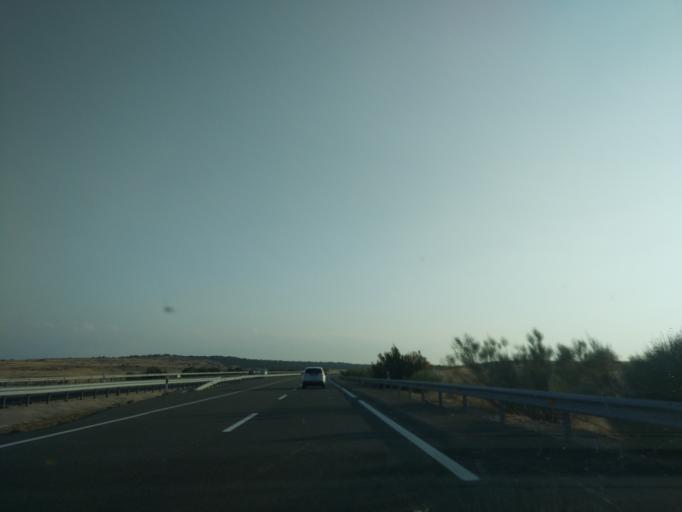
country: ES
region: Castille and Leon
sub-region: Provincia de Avila
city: Berrocalejo de Aragona
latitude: 40.6811
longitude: -4.6029
